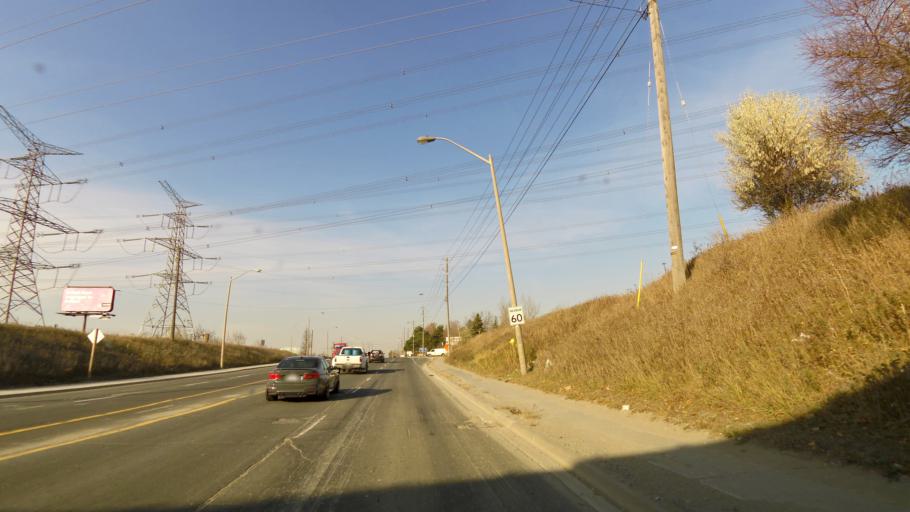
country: CA
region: Ontario
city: Concord
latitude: 43.7797
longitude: -79.5209
